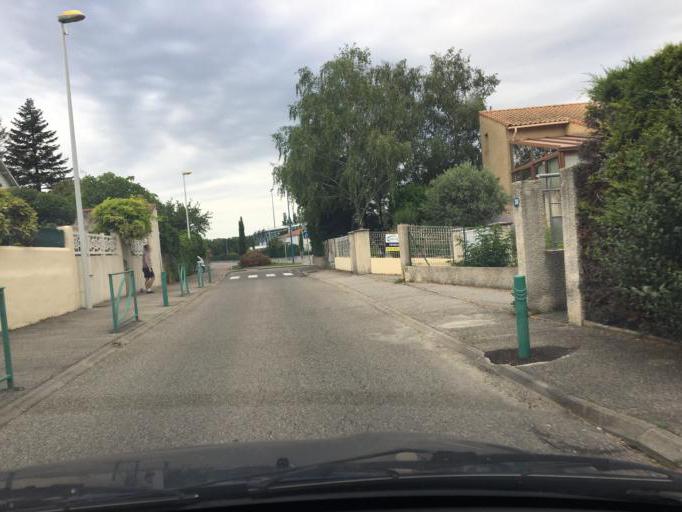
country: FR
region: Rhone-Alpes
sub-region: Departement de l'Ardeche
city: Guilherand-Granges
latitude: 44.9356
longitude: 4.8820
